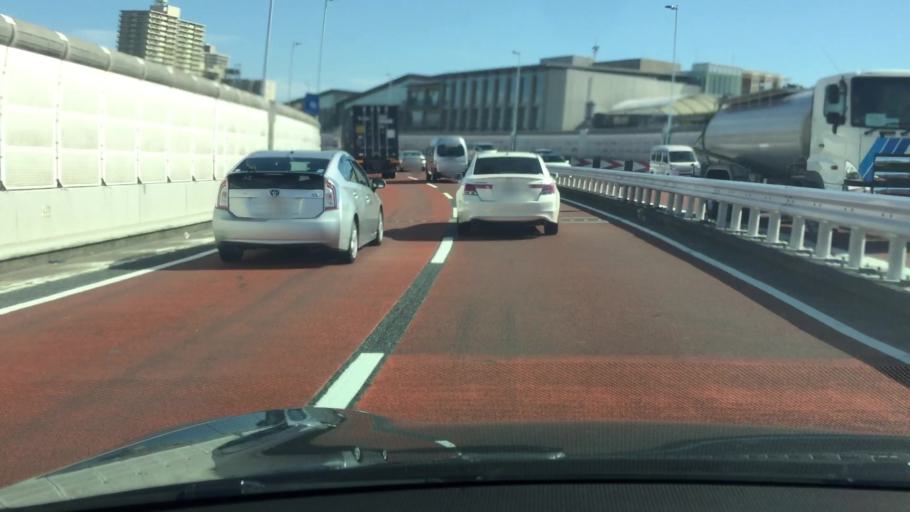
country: JP
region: Saitama
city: Shimotoda
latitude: 35.7790
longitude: 139.6737
